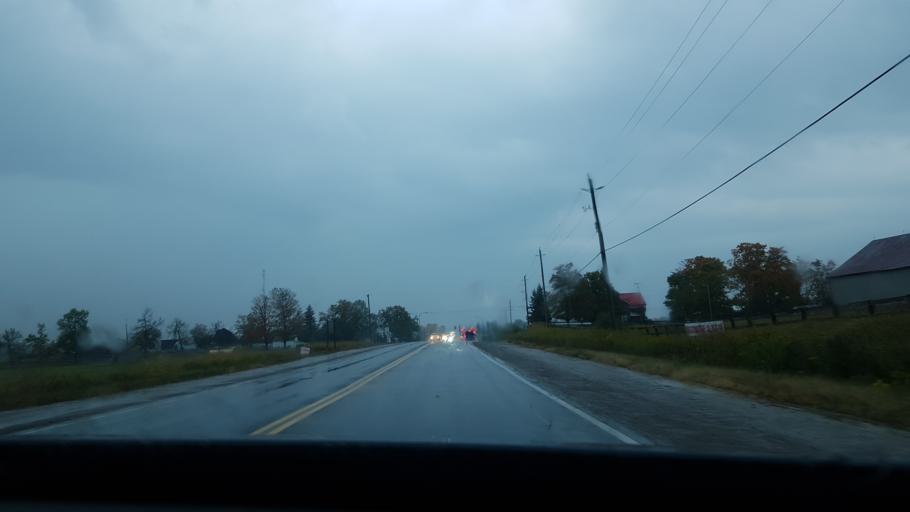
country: CA
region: Ontario
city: Peterborough
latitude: 44.3518
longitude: -78.3645
